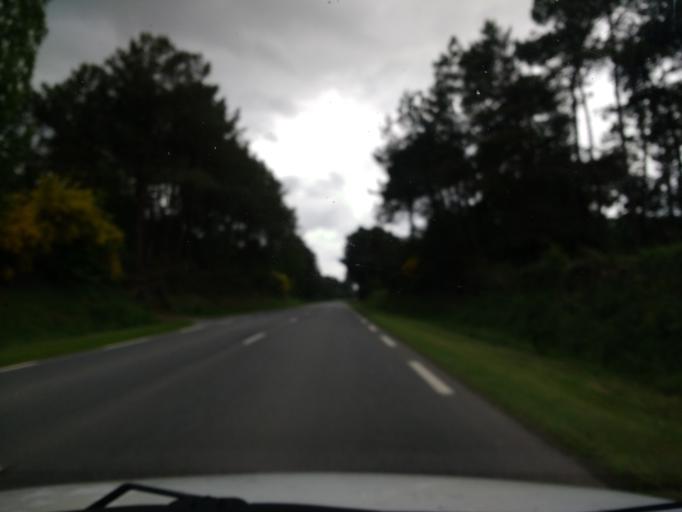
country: FR
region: Brittany
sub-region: Departement du Morbihan
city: Peaule
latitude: 47.5812
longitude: -2.3780
